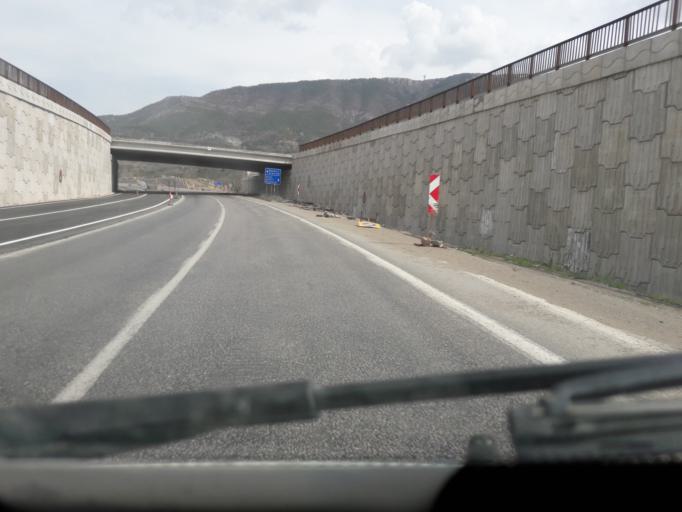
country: TR
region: Gumushane
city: Kale
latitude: 40.4064
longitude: 39.6065
